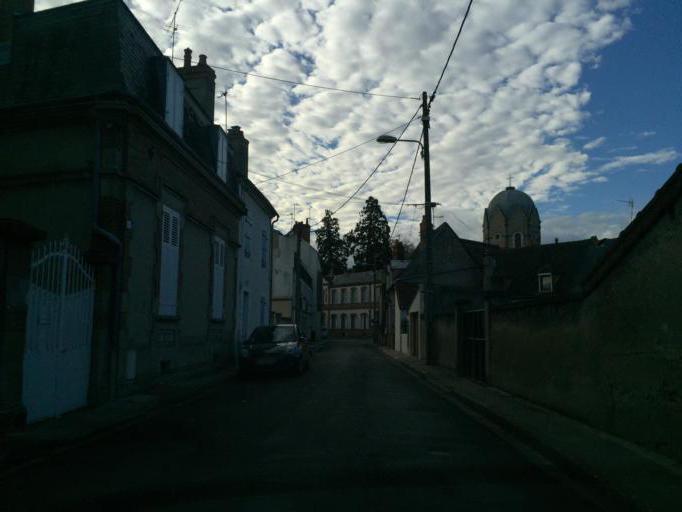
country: FR
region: Auvergne
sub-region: Departement de l'Allier
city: Moulins
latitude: 46.5718
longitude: 3.3335
